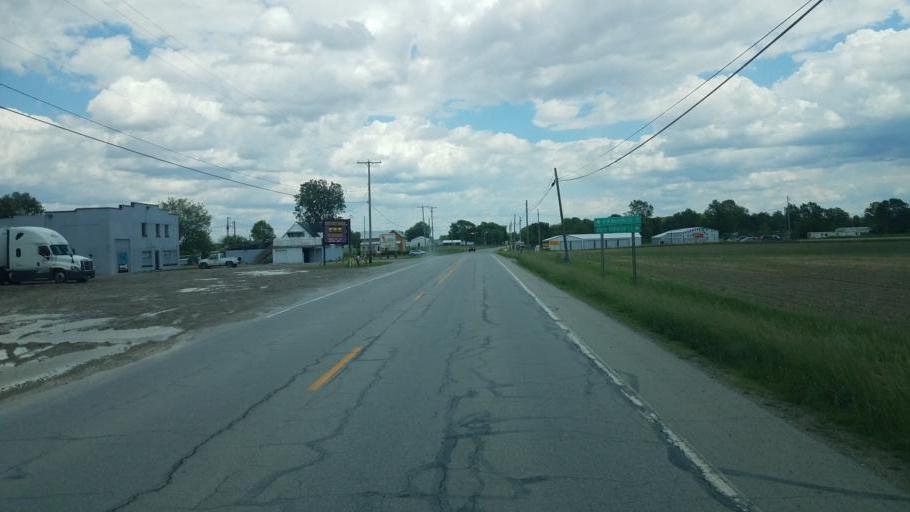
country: US
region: Ohio
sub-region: Crawford County
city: Galion
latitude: 40.8132
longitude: -82.8579
